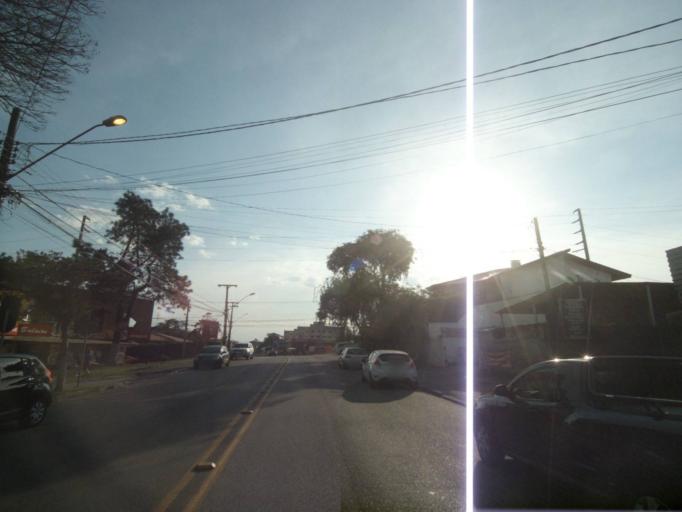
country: BR
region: Parana
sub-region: Curitiba
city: Curitiba
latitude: -25.4646
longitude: -49.3106
